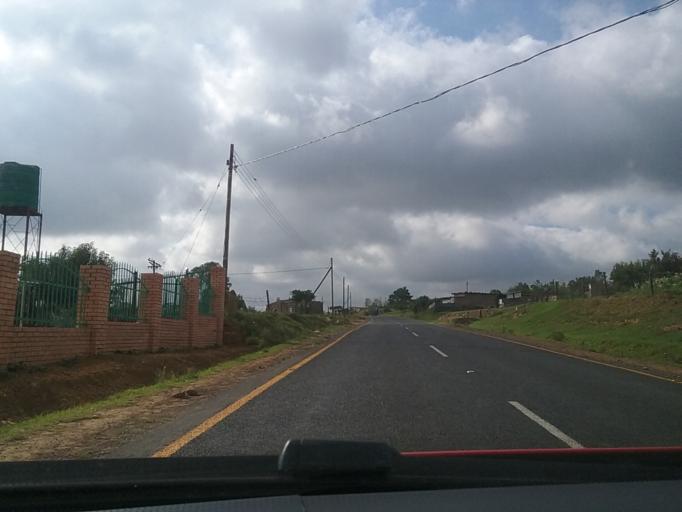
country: LS
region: Berea
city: Teyateyaneng
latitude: -29.1613
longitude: 27.7664
